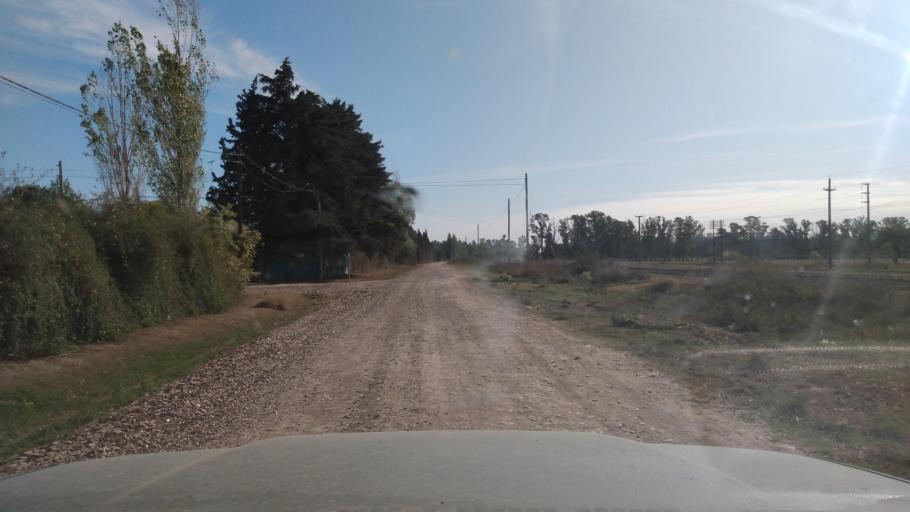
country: AR
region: Buenos Aires
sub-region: Partido de Lujan
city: Lujan
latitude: -34.5914
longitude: -59.1445
